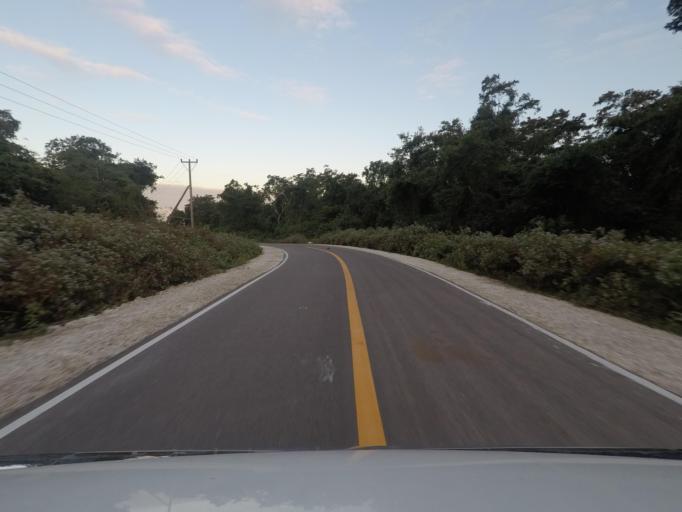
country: TL
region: Lautem
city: Lospalos
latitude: -8.4009
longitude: 127.2822
